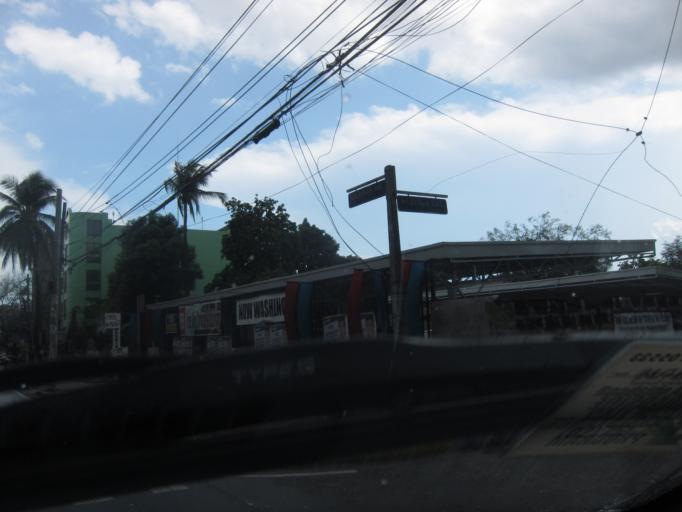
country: PH
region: Metro Manila
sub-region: Quezon City
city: Quezon City
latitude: 14.6443
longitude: 121.0537
